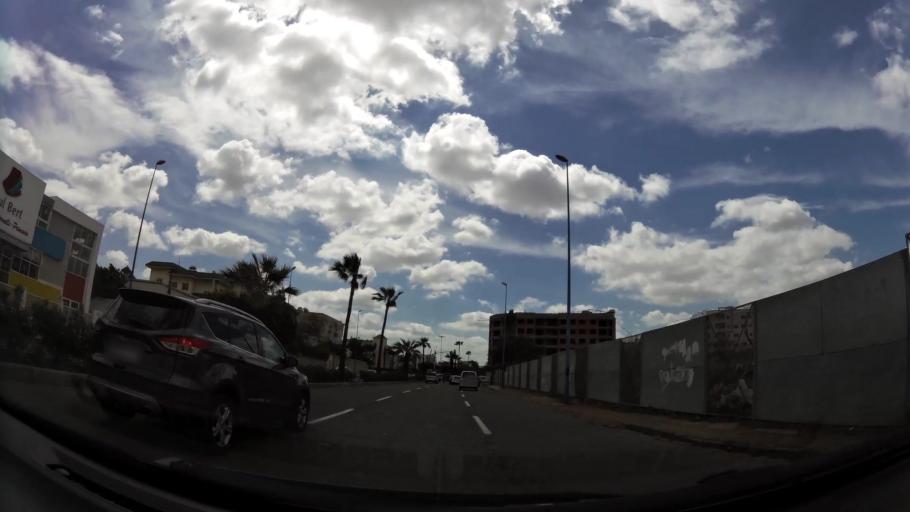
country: MA
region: Grand Casablanca
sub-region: Casablanca
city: Casablanca
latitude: 33.5582
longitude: -7.6250
